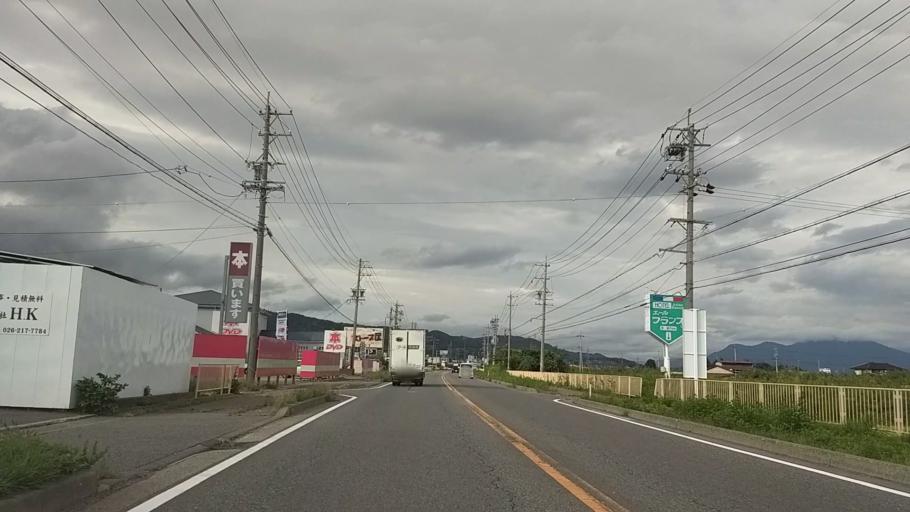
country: JP
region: Nagano
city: Suzaka
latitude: 36.6929
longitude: 138.2687
